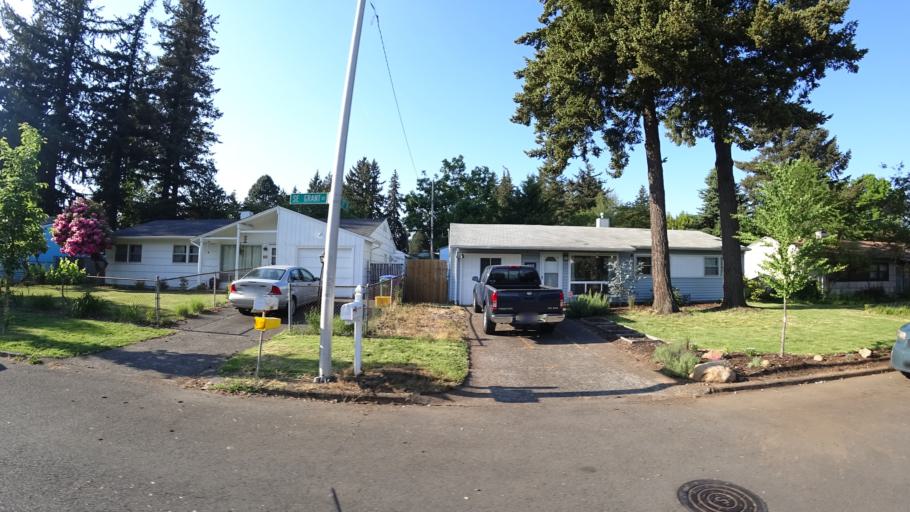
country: US
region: Oregon
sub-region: Multnomah County
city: Lents
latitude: 45.5070
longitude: -122.5120
